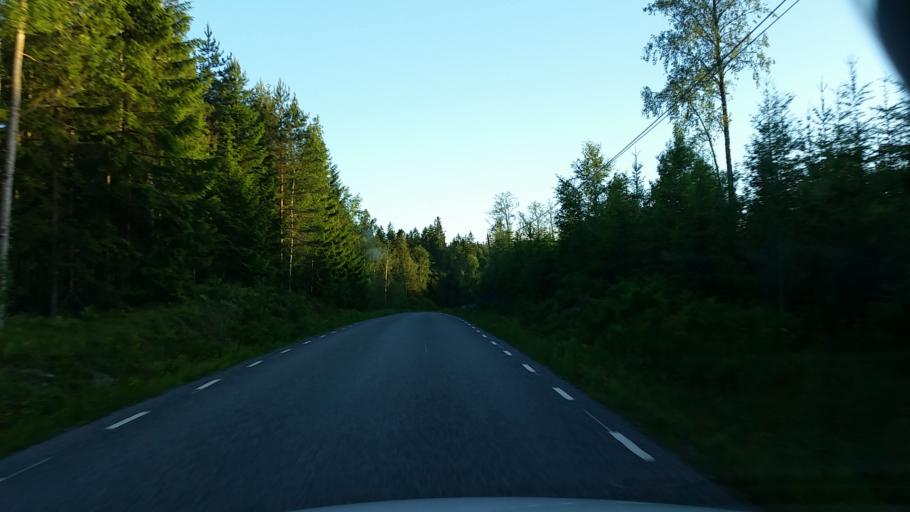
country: SE
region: Vaestmanland
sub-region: Kopings Kommun
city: Kolsva
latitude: 59.6056
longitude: 15.8731
